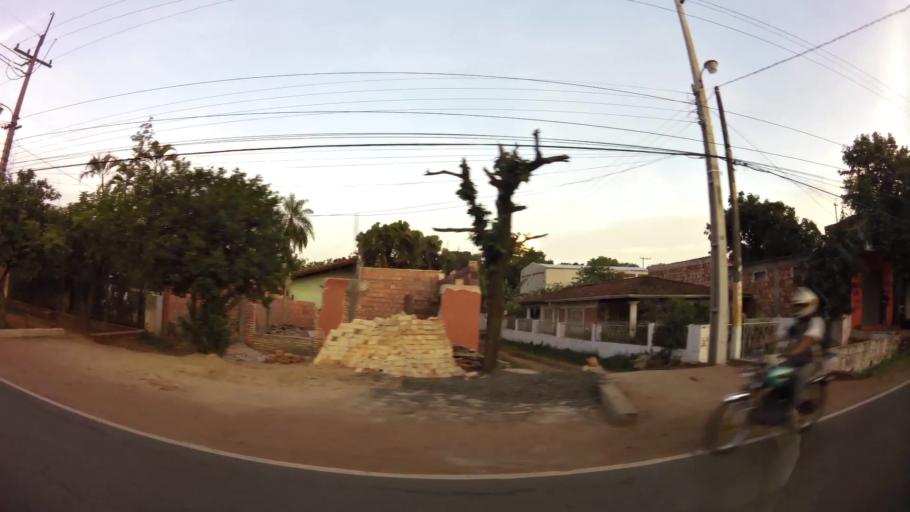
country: PY
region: Central
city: San Lorenzo
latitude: -25.3805
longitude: -57.4938
